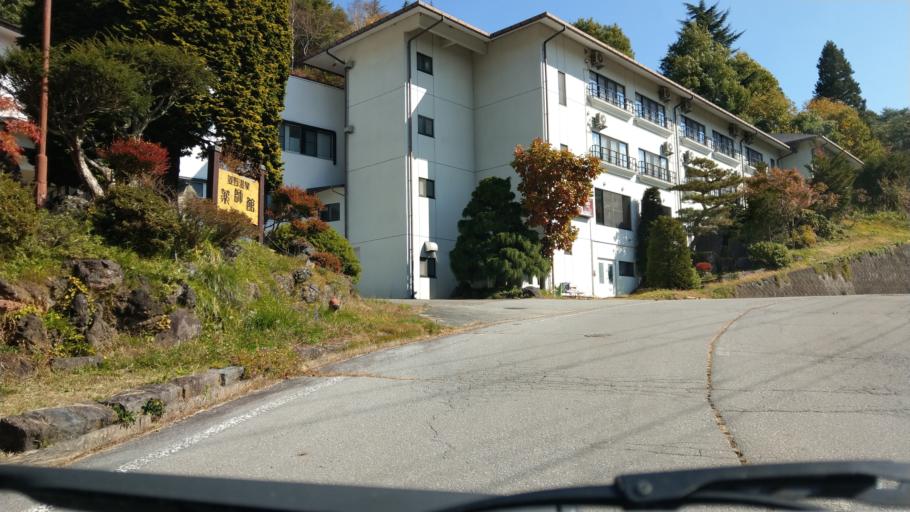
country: JP
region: Nagano
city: Komoro
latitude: 36.3632
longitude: 138.4475
